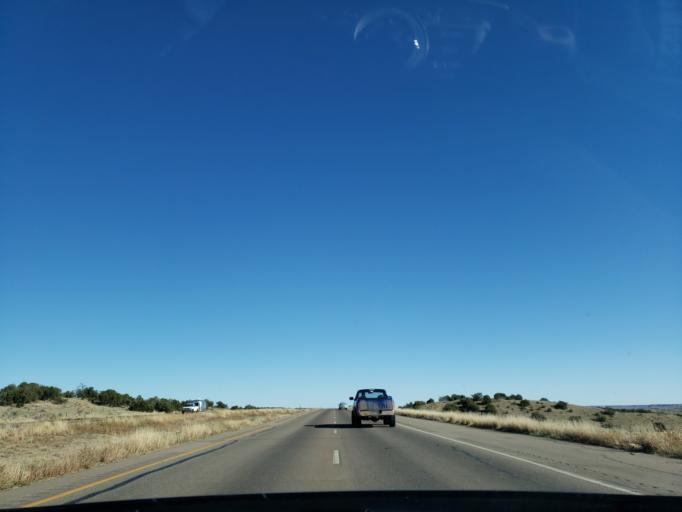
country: US
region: Colorado
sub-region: Fremont County
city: Florence
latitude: 38.4465
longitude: -105.1499
